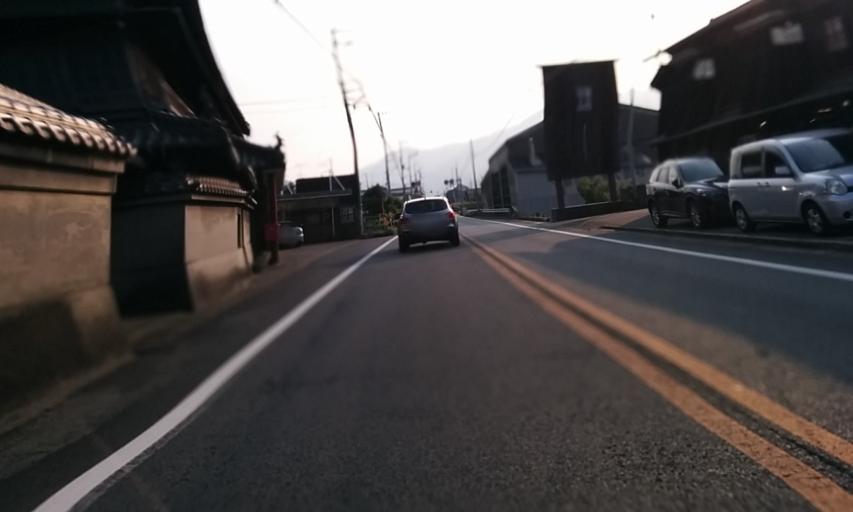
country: JP
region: Ehime
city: Saijo
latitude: 33.8719
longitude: 133.0577
